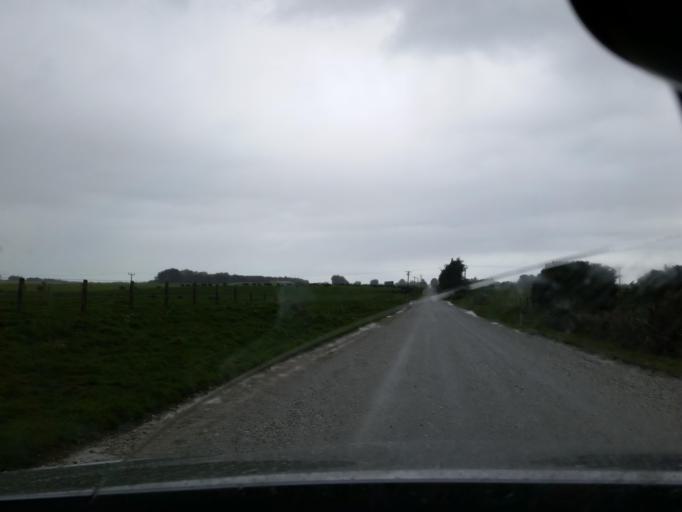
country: NZ
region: Southland
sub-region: Invercargill City
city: Invercargill
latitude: -46.4367
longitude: 168.5062
